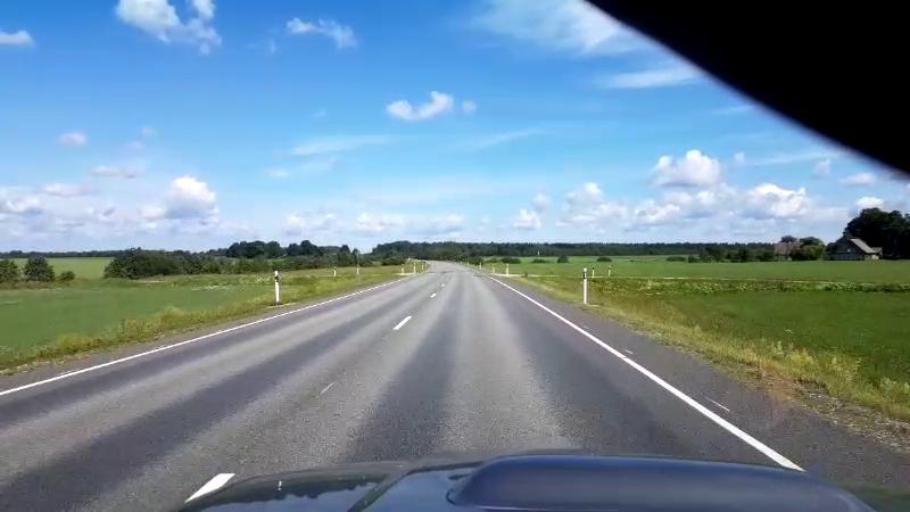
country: EE
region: Jaervamaa
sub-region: Jaerva-Jaani vald
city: Jarva-Jaani
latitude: 59.1485
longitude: 25.7704
